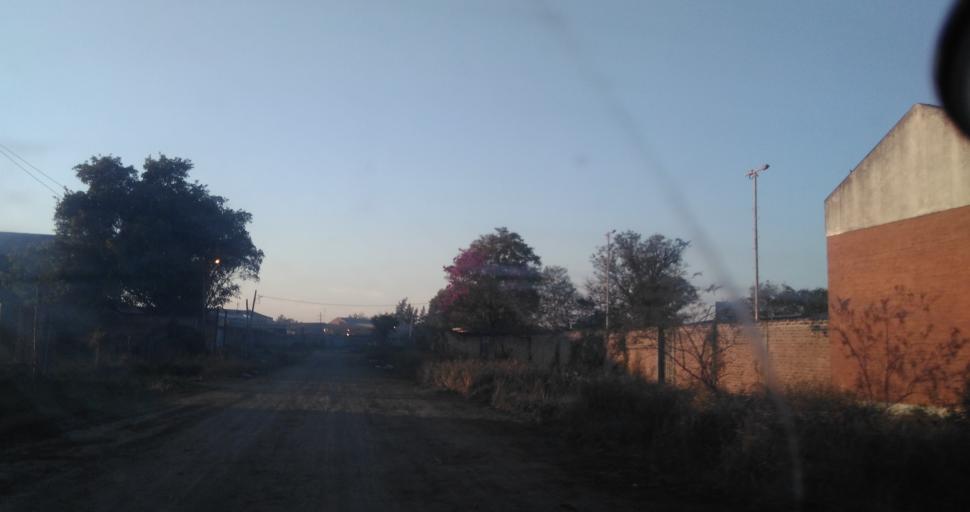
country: AR
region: Chaco
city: Fontana
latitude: -27.4238
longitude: -59.0126
